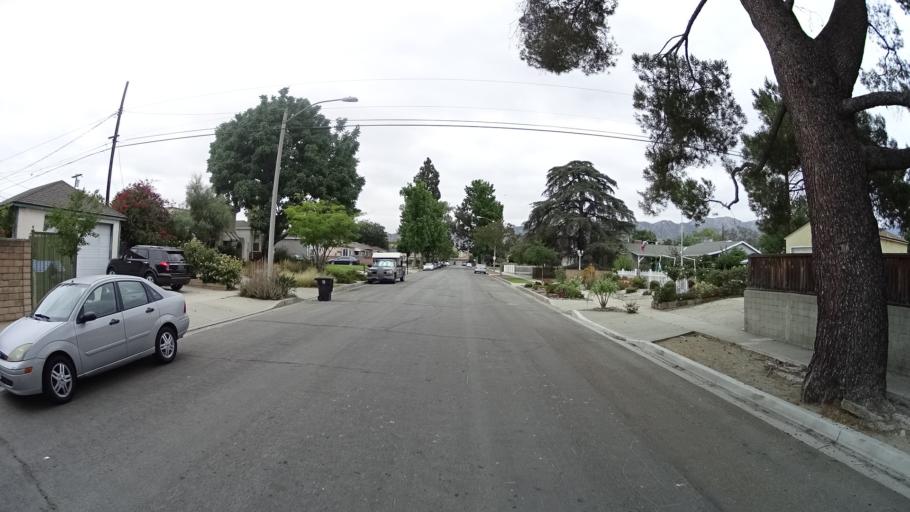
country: US
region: California
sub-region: Los Angeles County
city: Burbank
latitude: 34.1866
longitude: -118.3336
